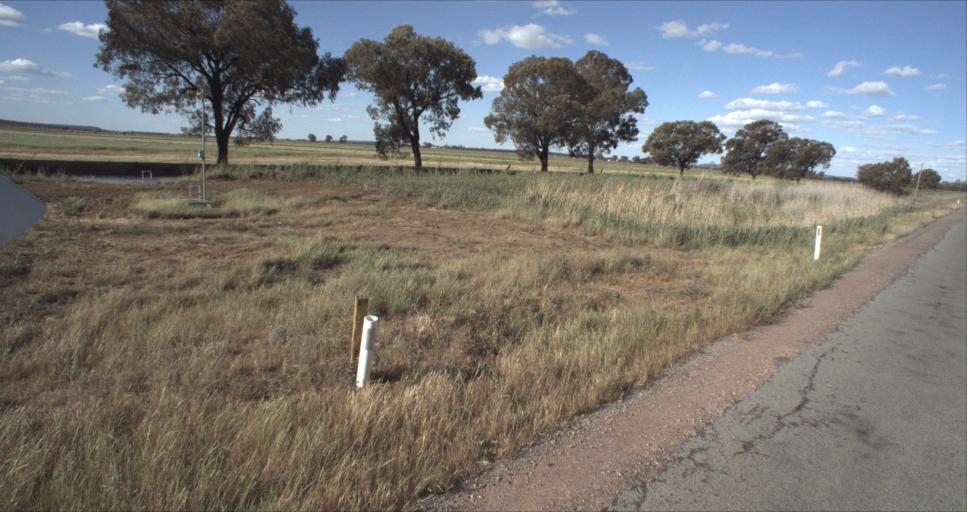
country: AU
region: New South Wales
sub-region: Leeton
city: Leeton
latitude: -34.4588
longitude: 146.2623
